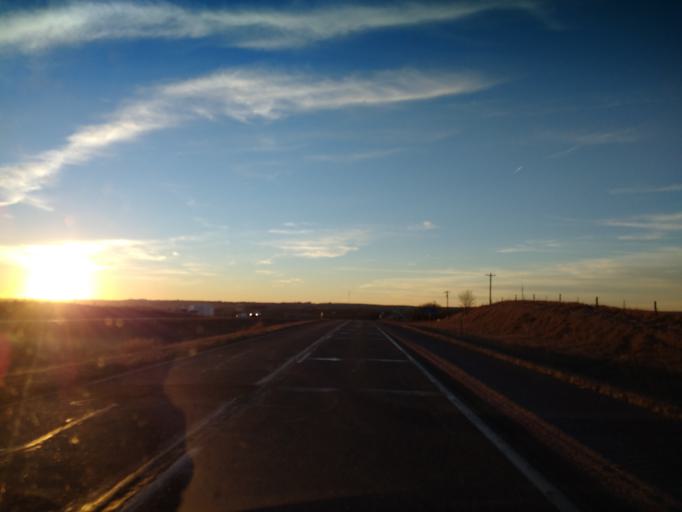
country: US
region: Iowa
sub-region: Woodbury County
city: Moville
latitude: 42.4821
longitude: -96.0535
